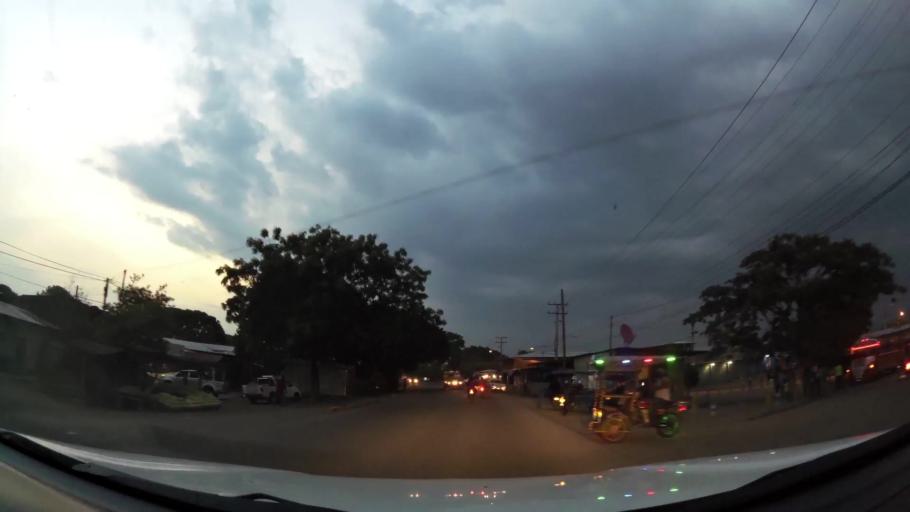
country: NI
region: Matagalpa
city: Ciudad Dario
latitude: 12.8558
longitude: -86.0999
